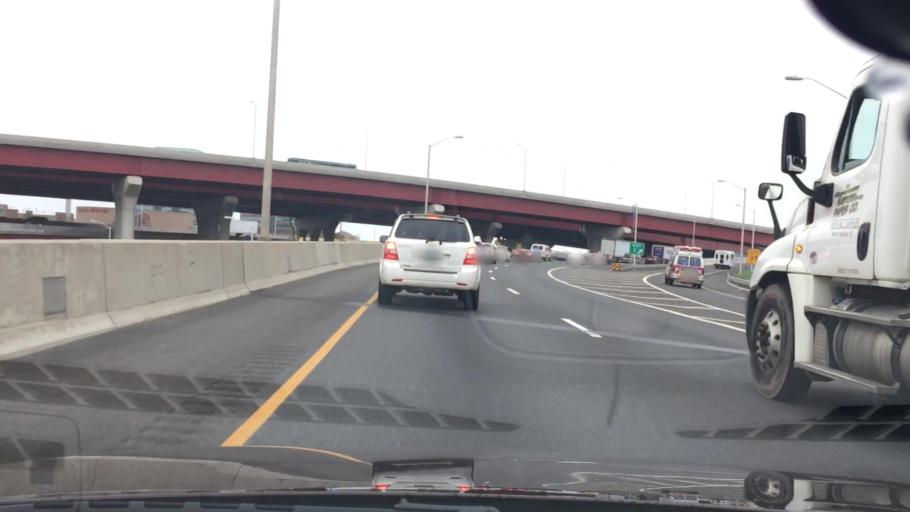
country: US
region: Connecticut
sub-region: New Haven County
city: New Haven
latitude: 41.3028
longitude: -72.9142
